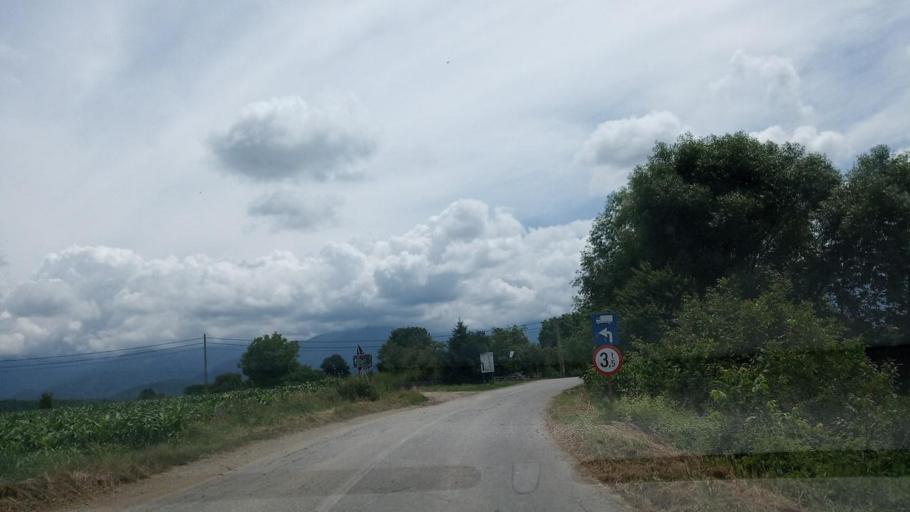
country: RO
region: Sibiu
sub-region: Comuna Porumbacu de Jos
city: Porumbacu de Jos
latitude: 45.7192
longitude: 24.4751
